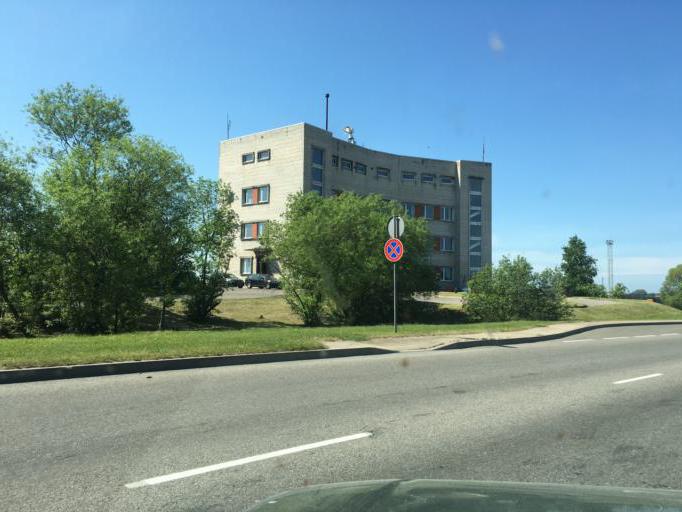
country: LV
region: Ventspils
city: Ventspils
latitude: 57.3967
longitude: 21.6152
